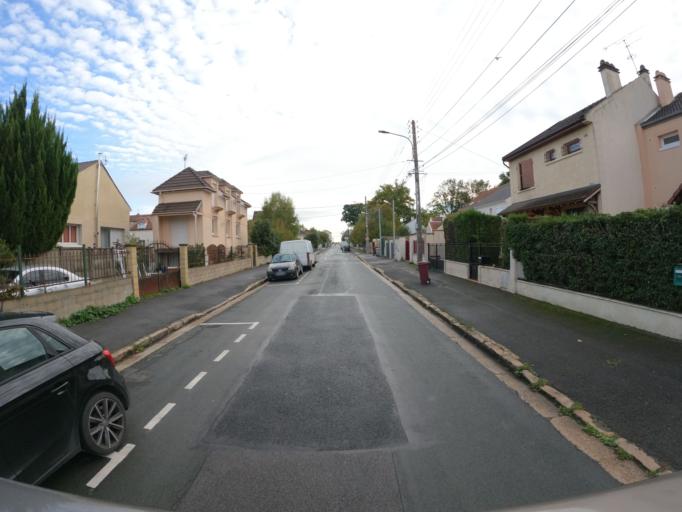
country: FR
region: Ile-de-France
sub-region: Departement de Seine-Saint-Denis
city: Montfermeil
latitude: 48.8996
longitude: 2.5980
